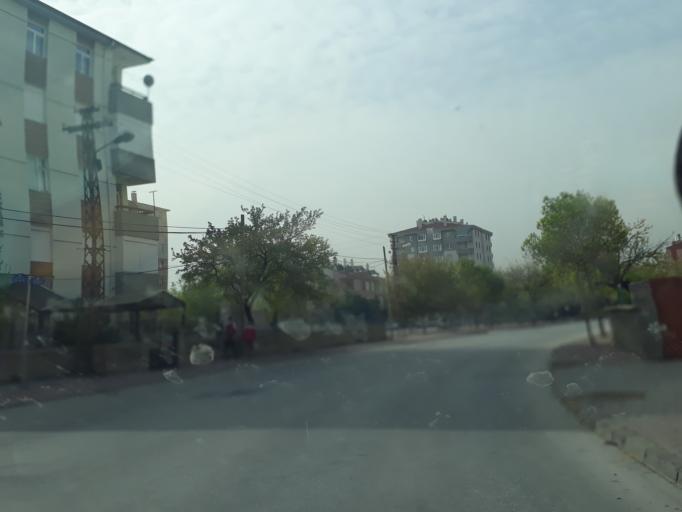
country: TR
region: Konya
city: Selcuklu
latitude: 37.9352
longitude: 32.4996
